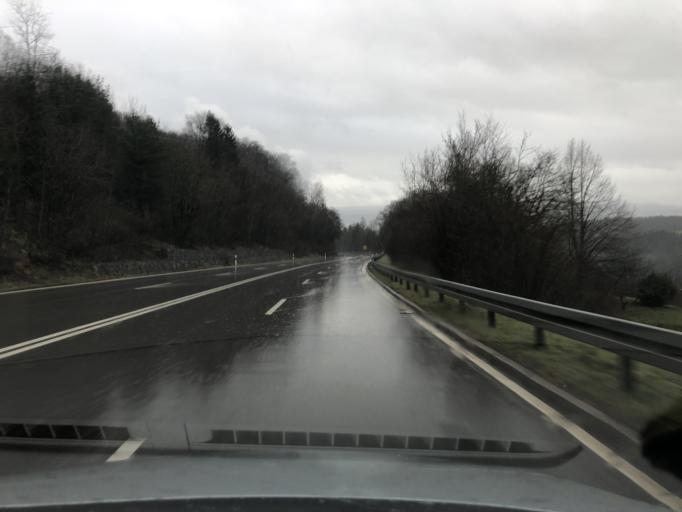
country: DE
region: Baden-Wuerttemberg
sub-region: Freiburg Region
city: Dogern
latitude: 47.6307
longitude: 8.1841
